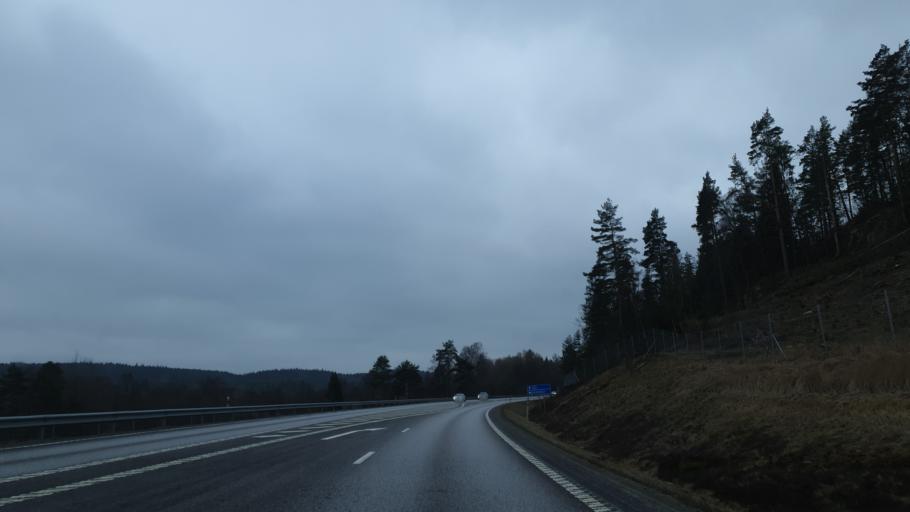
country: SE
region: Vaestra Goetaland
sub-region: Boras Kommun
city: Viskafors
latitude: 57.5785
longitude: 12.8576
